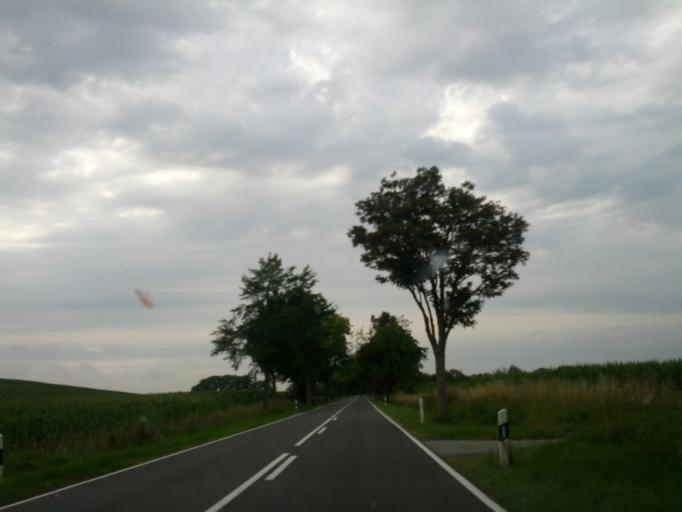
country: DE
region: Mecklenburg-Vorpommern
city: Satow-Oberhagen
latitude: 54.0027
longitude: 11.8315
